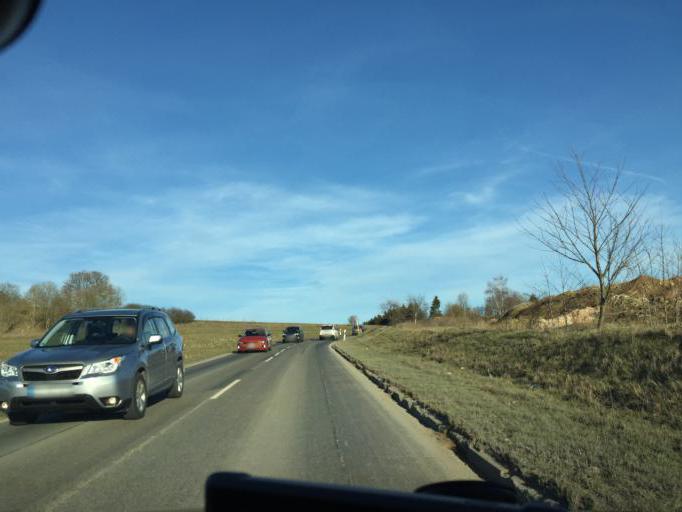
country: DE
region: Rheinland-Pfalz
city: Niederahr
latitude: 50.4765
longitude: 7.8663
